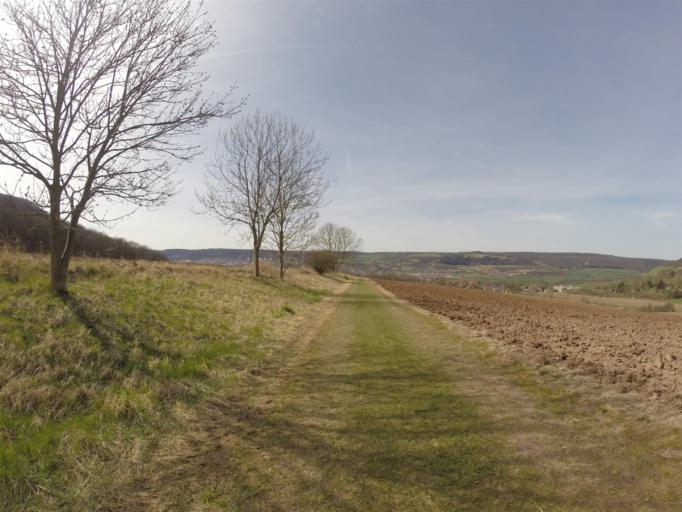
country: DE
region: Thuringia
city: Golmsdorf
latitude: 50.9481
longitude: 11.6474
